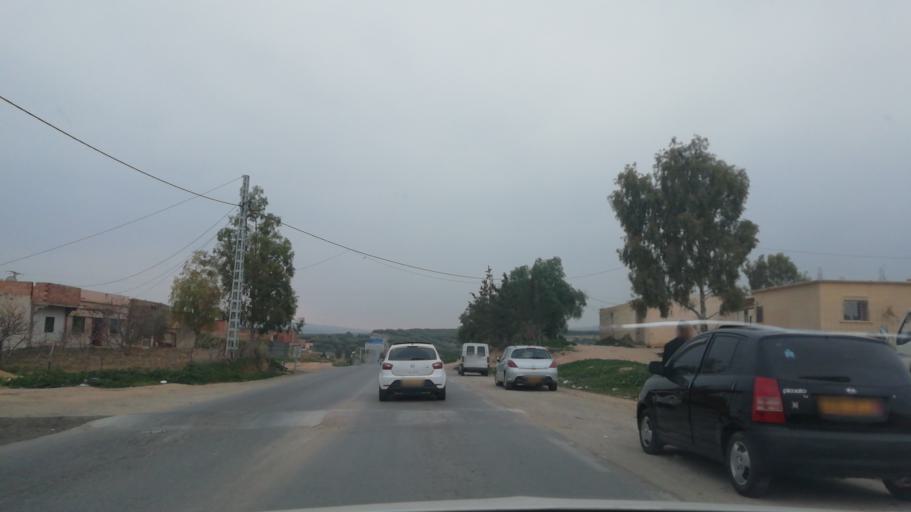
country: DZ
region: Mascara
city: Bou Hanifia el Hamamat
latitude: 35.2838
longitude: -0.1470
